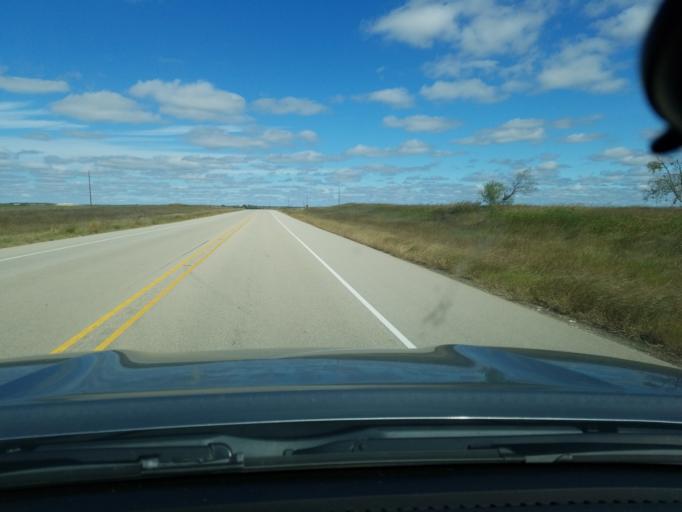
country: US
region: Texas
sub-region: Hamilton County
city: Hamilton
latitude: 31.6276
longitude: -98.1540
